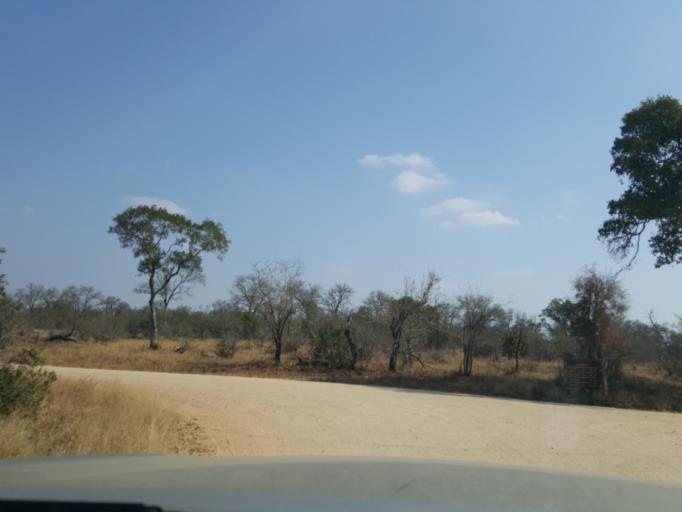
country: ZA
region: Mpumalanga
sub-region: Ehlanzeni District
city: Komatipoort
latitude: -25.2735
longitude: 31.7789
